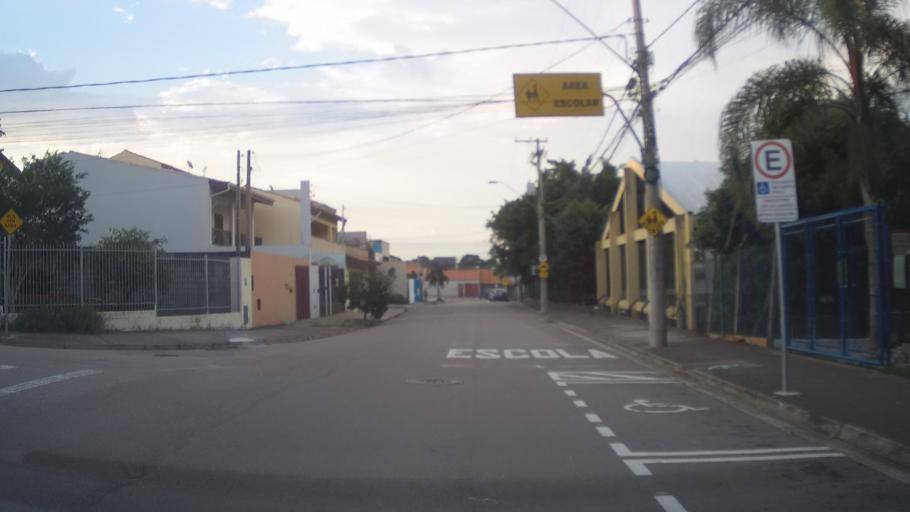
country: BR
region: Sao Paulo
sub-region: Jundiai
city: Jundiai
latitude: -23.1907
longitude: -46.9613
